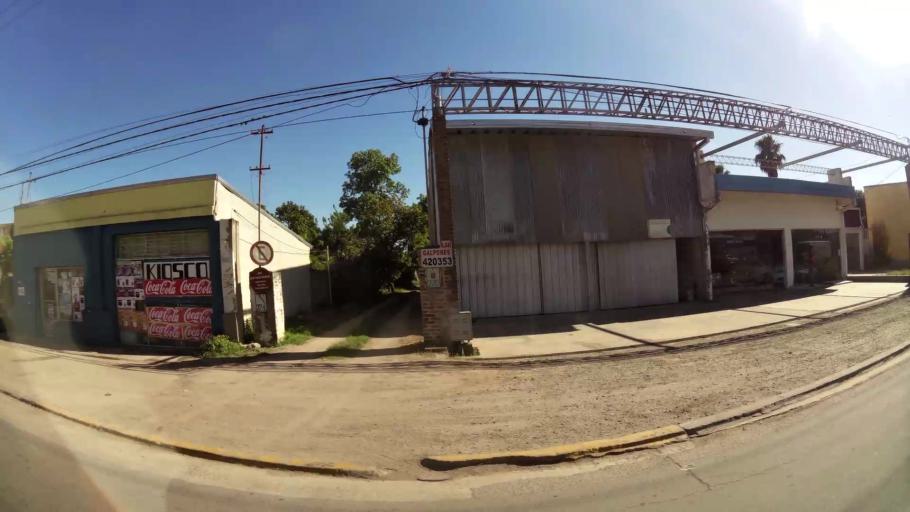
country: AR
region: Santa Fe
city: Esperanza
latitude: -31.4462
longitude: -60.9146
